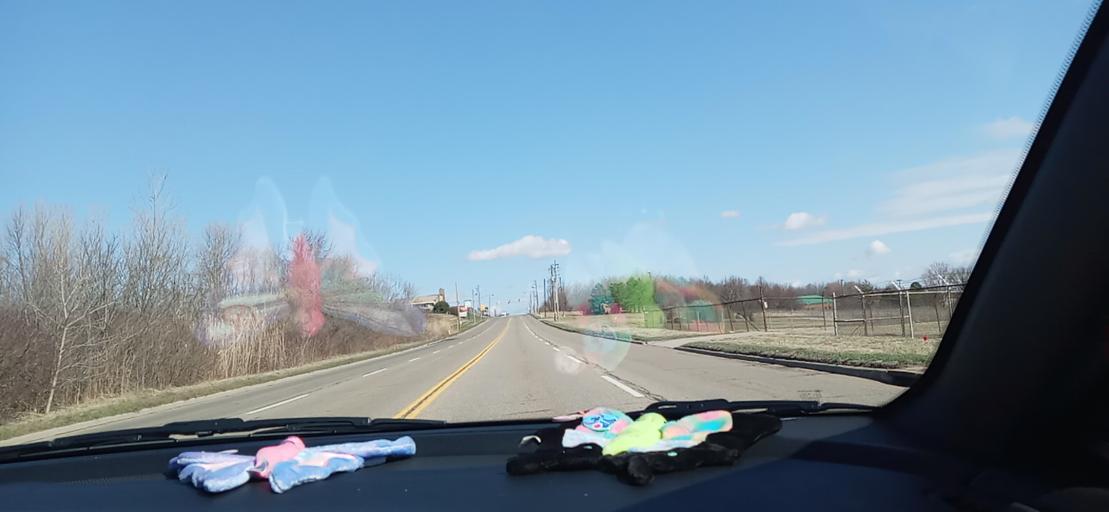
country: US
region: Ohio
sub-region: Summit County
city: Sawyerwood
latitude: 41.0323
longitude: -81.4819
